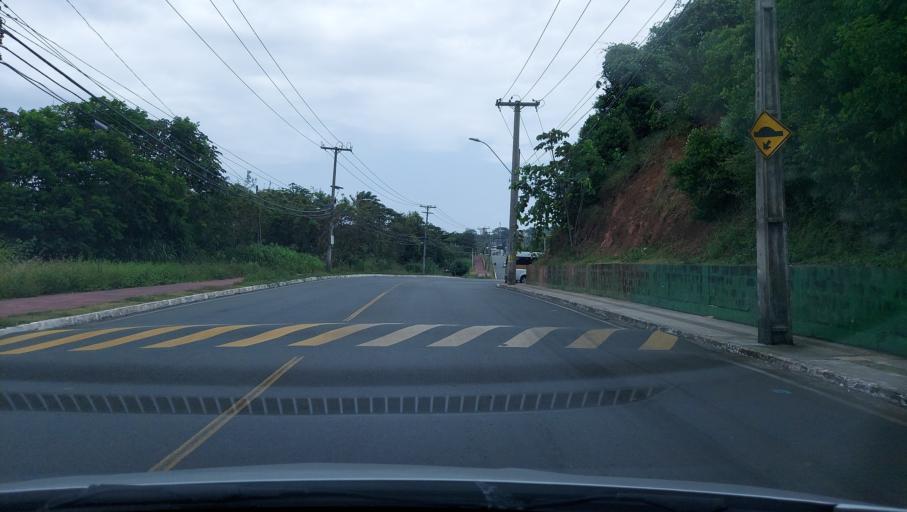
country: BR
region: Bahia
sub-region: Lauro De Freitas
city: Lauro de Freitas
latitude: -12.9501
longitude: -38.3883
